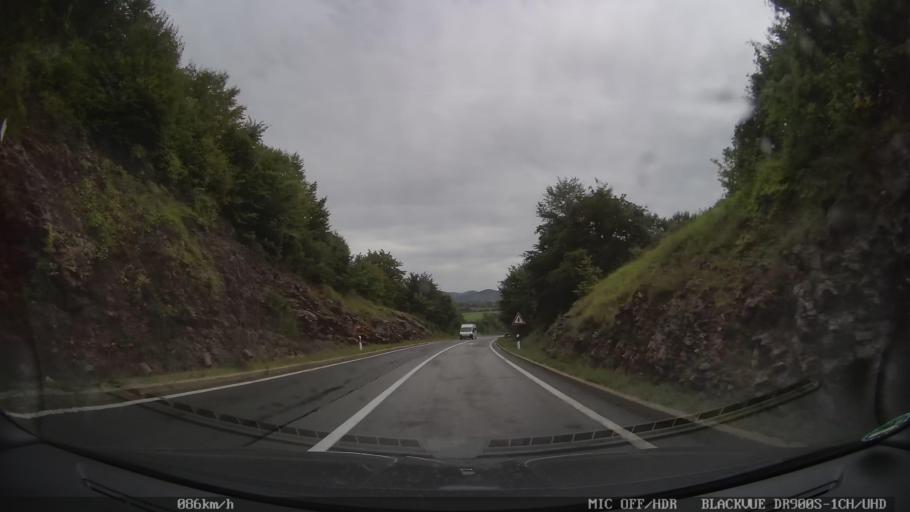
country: HR
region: Licko-Senjska
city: Brinje
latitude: 44.9604
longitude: 15.0916
